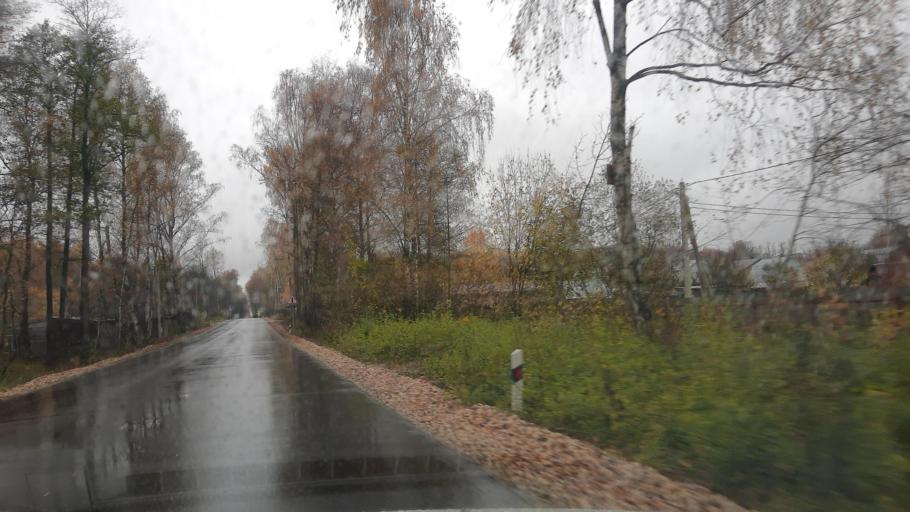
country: RU
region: Moskovskaya
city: Elektrostal'
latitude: 55.7962
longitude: 38.3711
